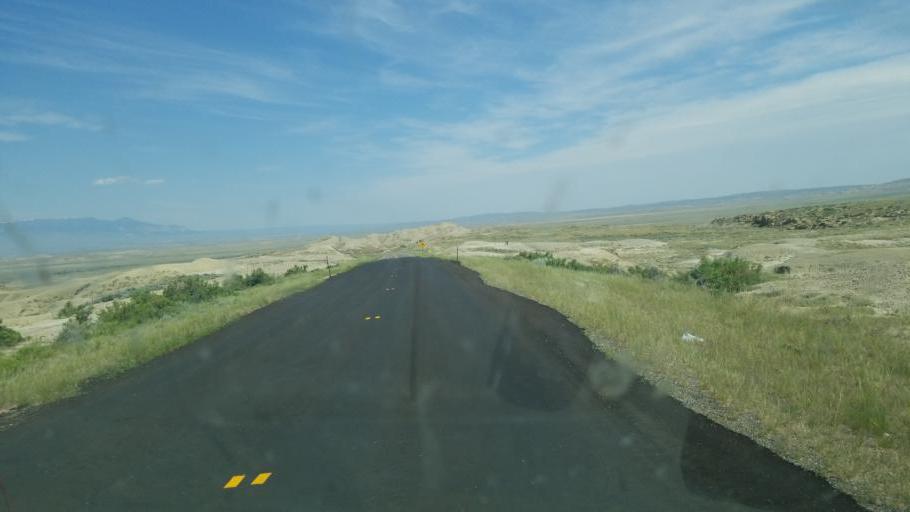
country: US
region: Wyoming
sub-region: Park County
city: Powell
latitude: 44.7853
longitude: -108.9347
